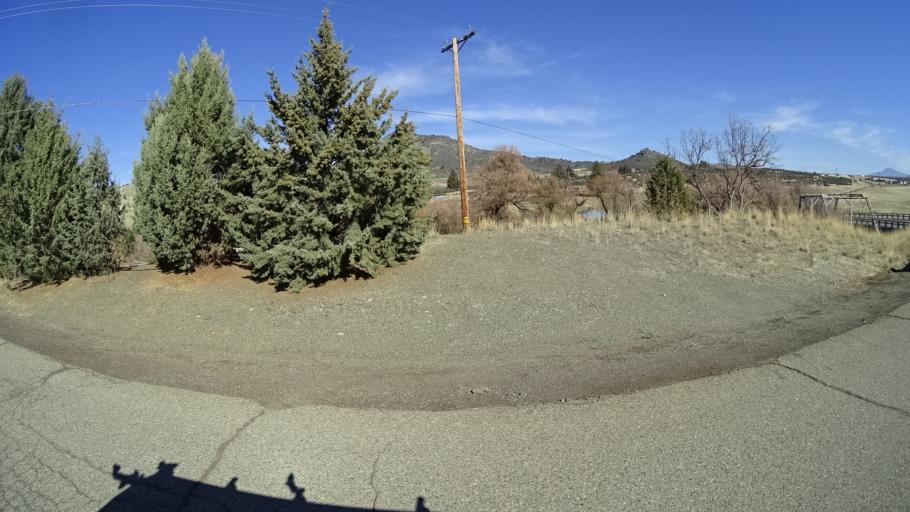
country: US
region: California
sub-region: Siskiyou County
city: Yreka
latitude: 41.7722
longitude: -122.5938
